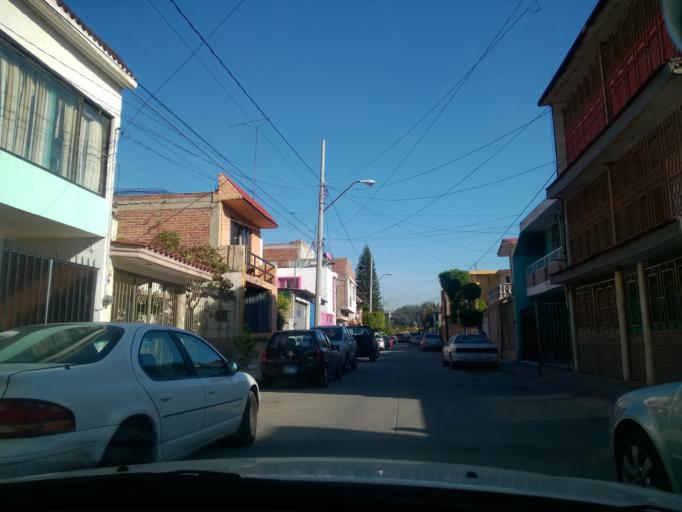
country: MX
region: Guanajuato
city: Leon
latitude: 21.1092
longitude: -101.6498
